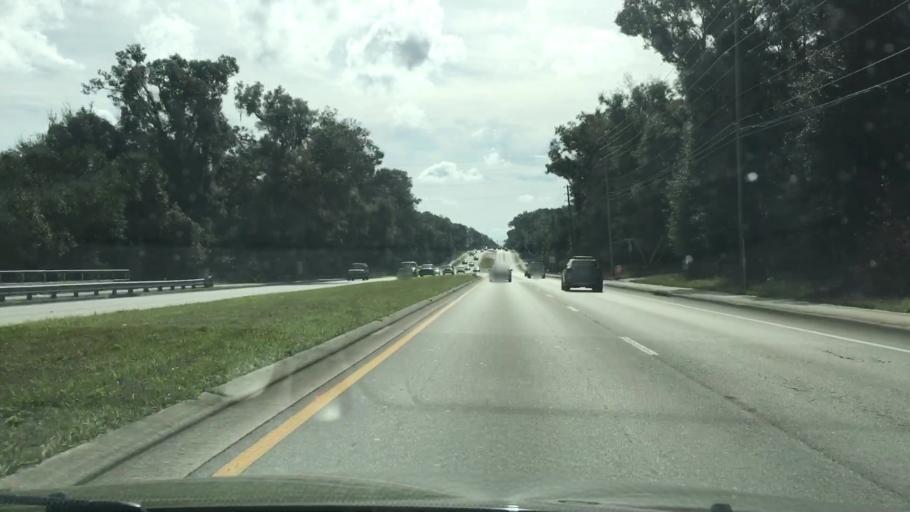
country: US
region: Florida
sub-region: Volusia County
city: North DeLand
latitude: 29.0484
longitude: -81.3249
